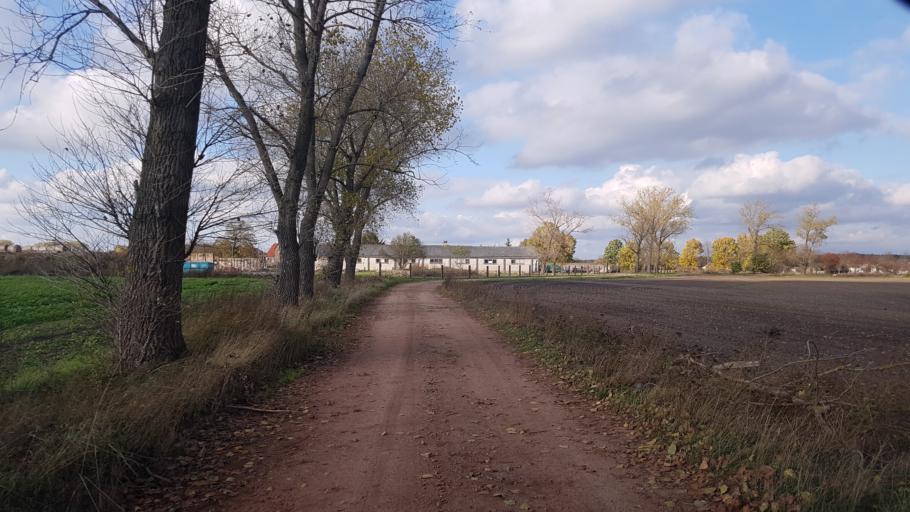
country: DE
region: Brandenburg
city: Schonewalde
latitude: 51.6914
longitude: 13.5732
